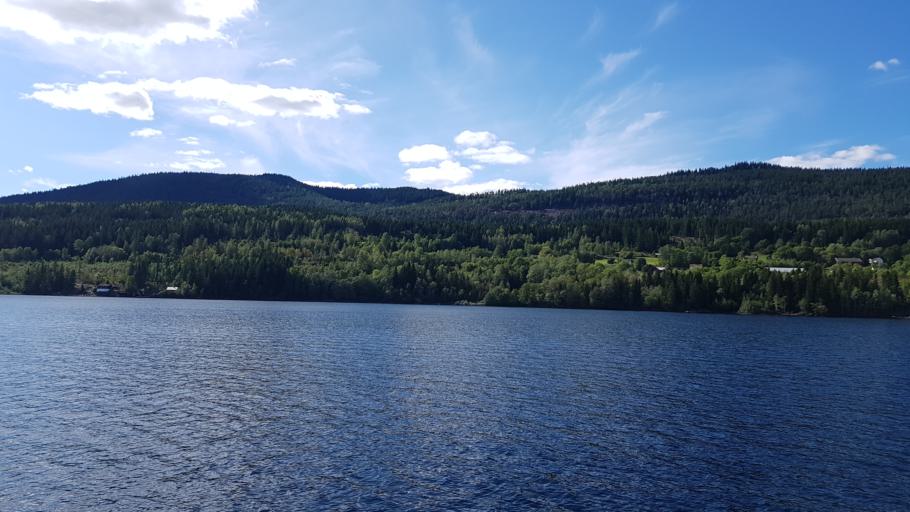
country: NO
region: Akershus
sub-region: Hurdal
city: Hurdal
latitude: 60.5376
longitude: 11.1995
